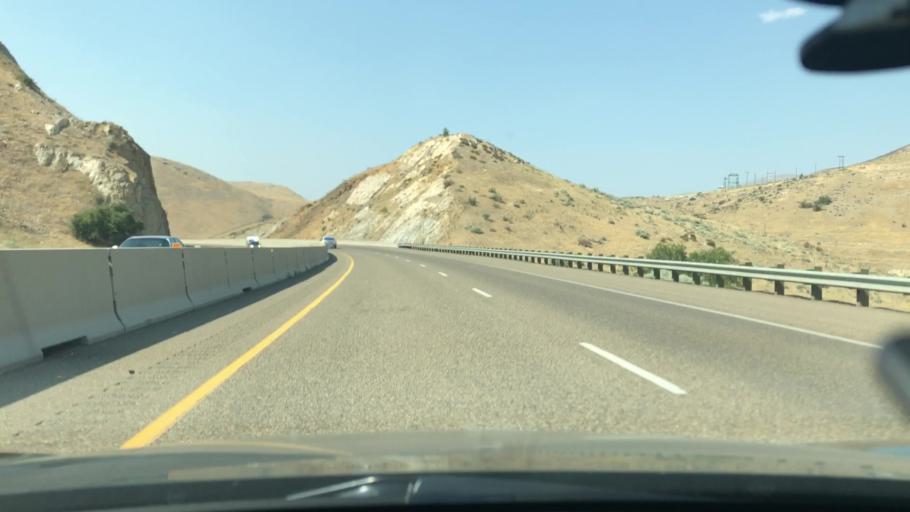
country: US
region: Idaho
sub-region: Washington County
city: Weiser
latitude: 44.4004
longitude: -117.3084
